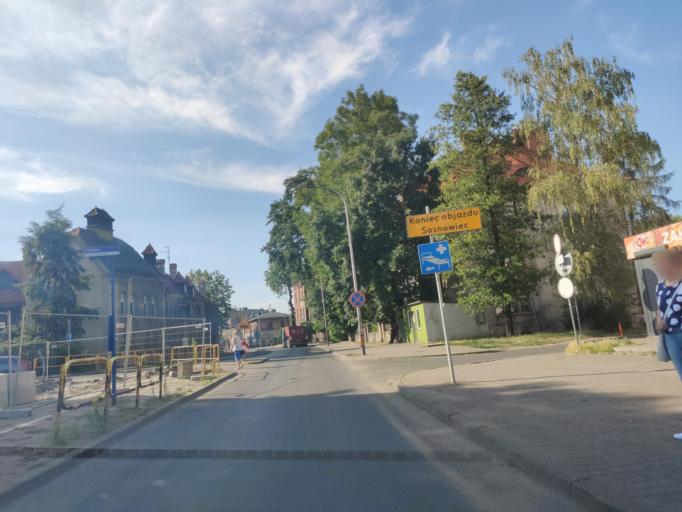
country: PL
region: Silesian Voivodeship
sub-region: Sosnowiec
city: Sosnowiec
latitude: 50.2475
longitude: 19.1336
